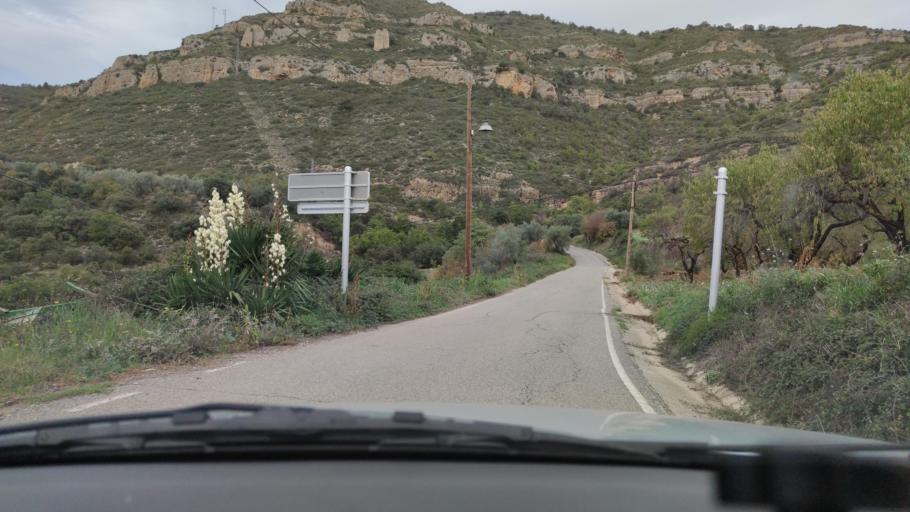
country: ES
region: Catalonia
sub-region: Provincia de Lleida
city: Llimiana
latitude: 42.0689
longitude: 0.9418
